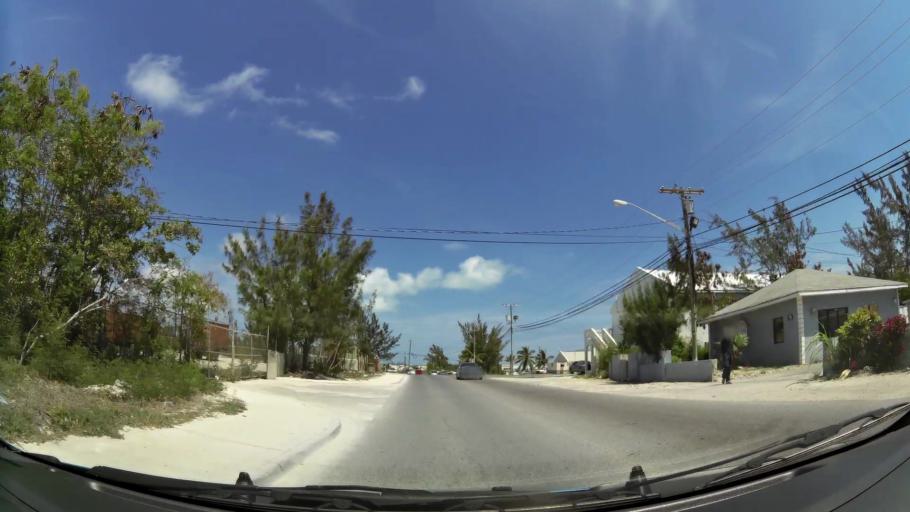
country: BS
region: Mayaguana
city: Abraham's Bay
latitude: 21.7694
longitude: -72.2577
